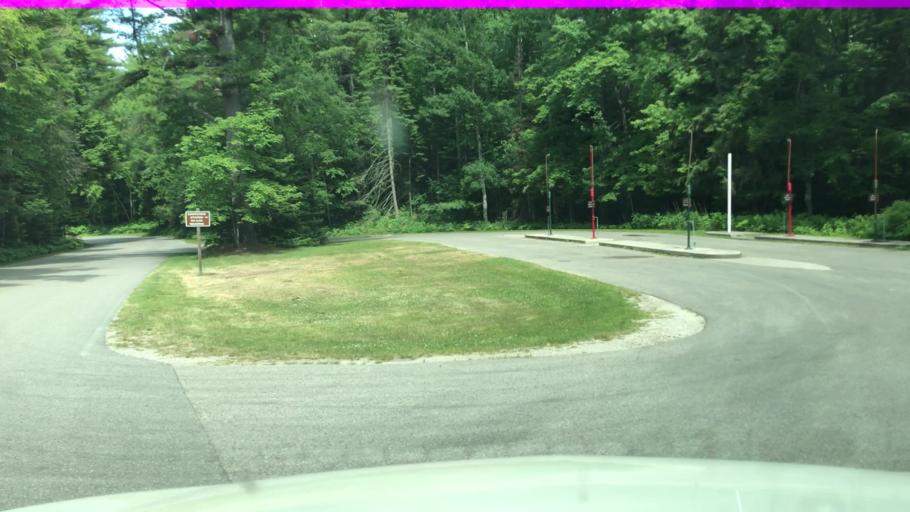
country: US
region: Michigan
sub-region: Schoolcraft County
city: Manistique
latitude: 45.9440
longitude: -86.3313
